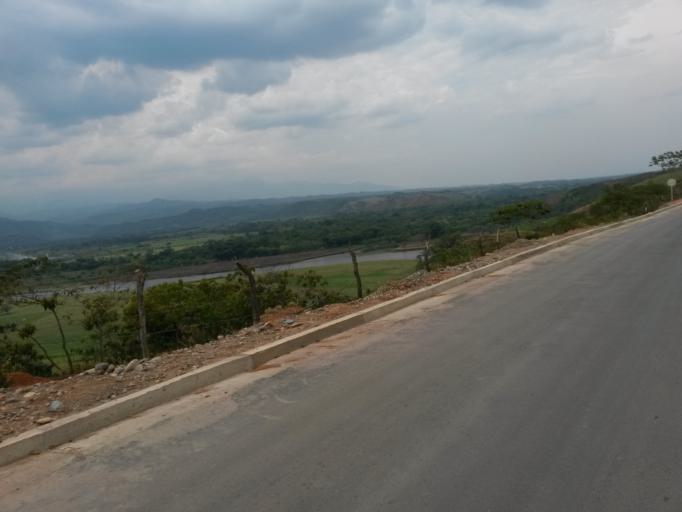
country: CO
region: Cauca
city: Buenos Aires
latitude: 3.0864
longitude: -76.6076
